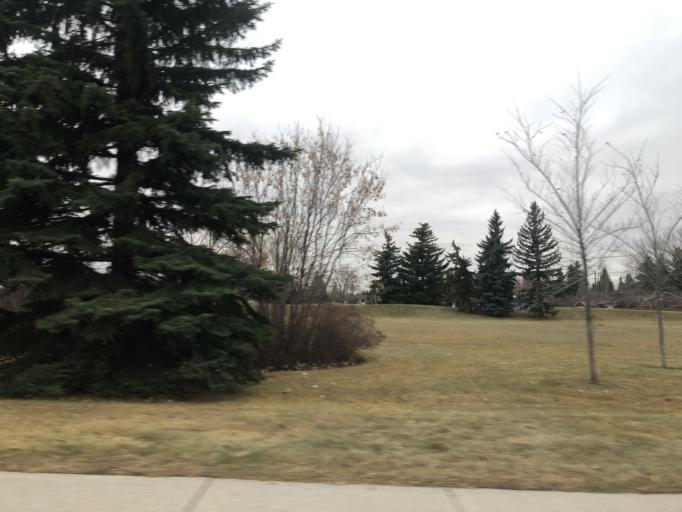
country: CA
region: Alberta
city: Calgary
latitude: 50.9380
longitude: -114.0421
